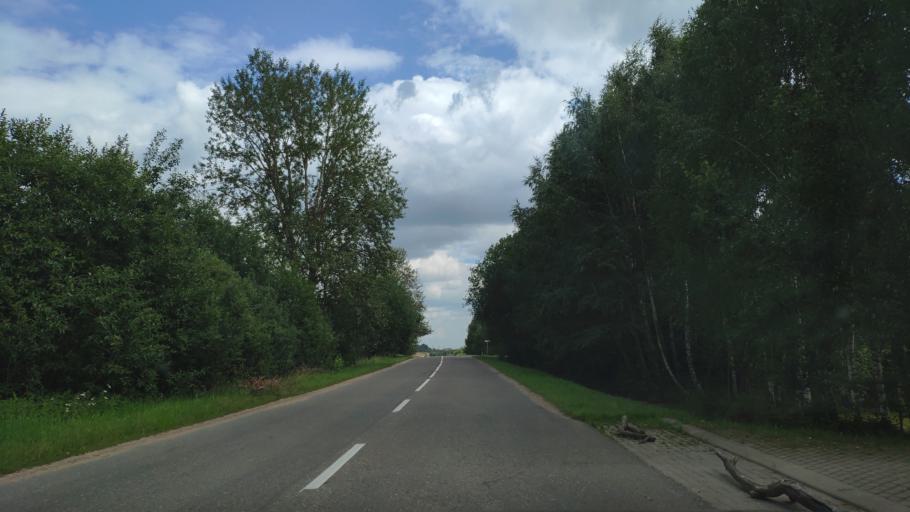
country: BY
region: Minsk
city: Khatsyezhyna
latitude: 53.8740
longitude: 27.2983
